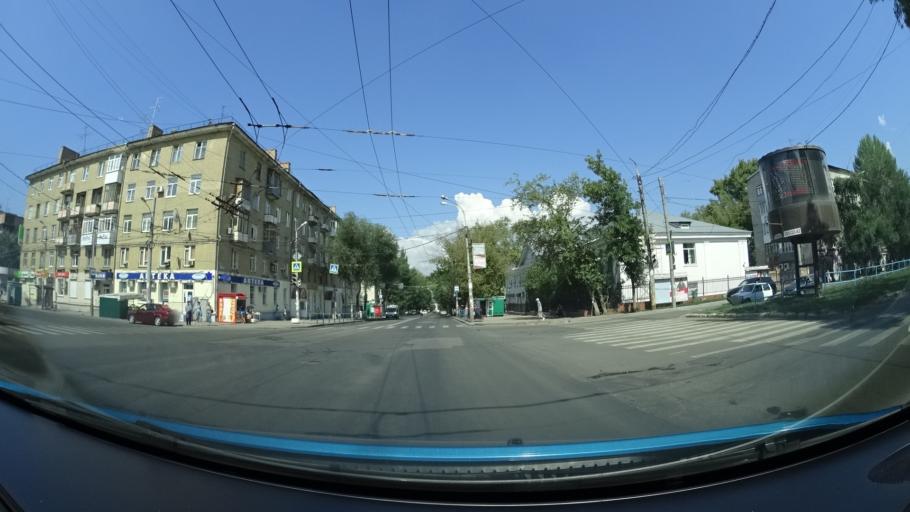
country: RU
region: Samara
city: Samara
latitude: 53.2109
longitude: 50.1562
